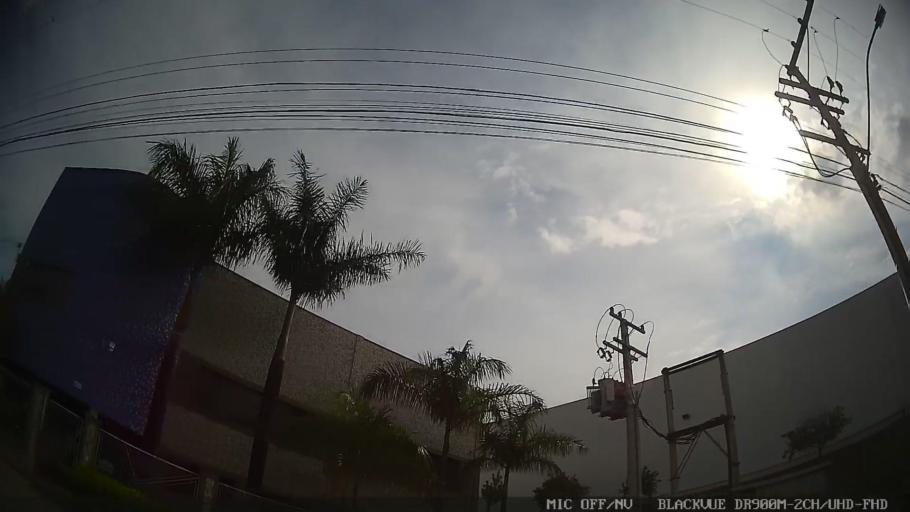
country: BR
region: Sao Paulo
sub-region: Braganca Paulista
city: Braganca Paulista
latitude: -22.9332
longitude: -46.5388
